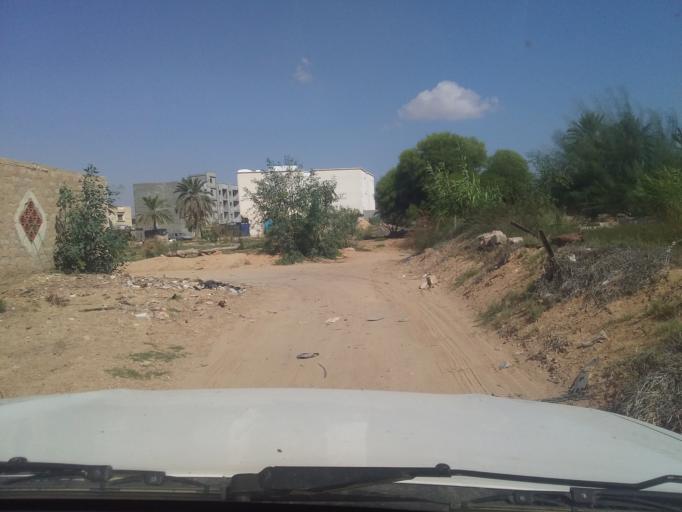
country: TN
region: Qabis
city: Gabes
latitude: 33.6277
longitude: 10.2821
